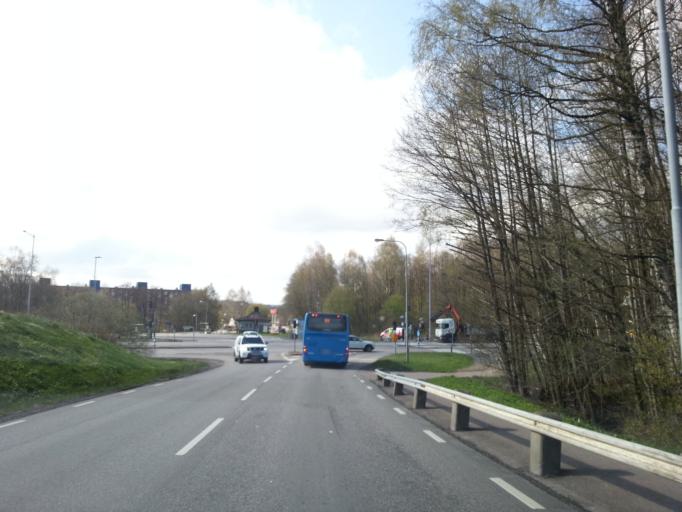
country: SE
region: Vaestra Goetaland
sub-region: Ale Kommun
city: Surte
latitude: 57.8011
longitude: 11.9921
